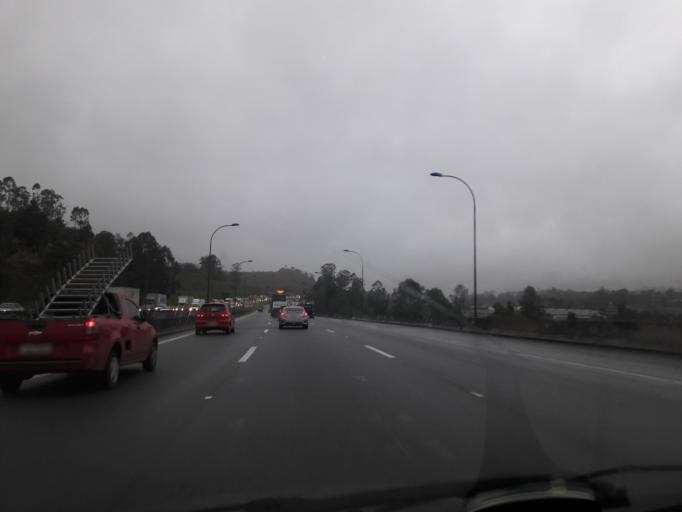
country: BR
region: Sao Paulo
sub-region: Embu
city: Embu
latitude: -23.6402
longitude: -46.8337
